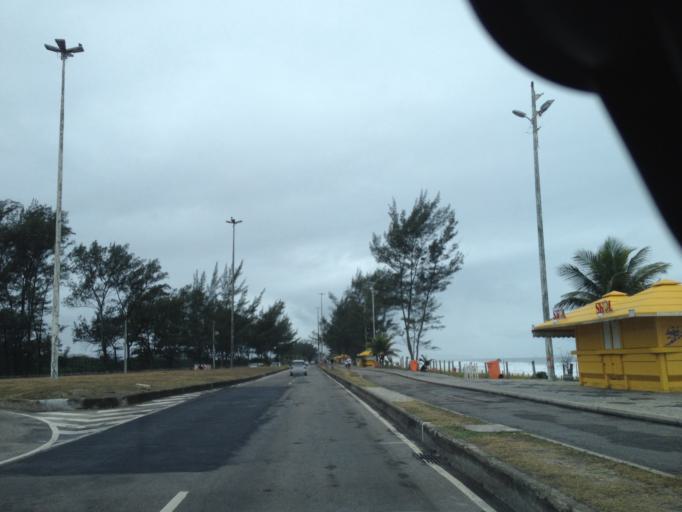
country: BR
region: Rio de Janeiro
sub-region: Nilopolis
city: Nilopolis
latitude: -23.0225
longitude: -43.4477
